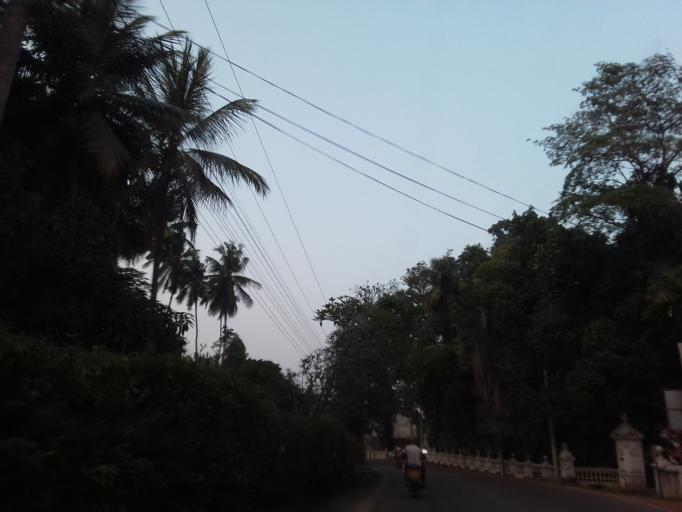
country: LK
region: Western
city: Welisara
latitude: 7.0419
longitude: 79.9575
